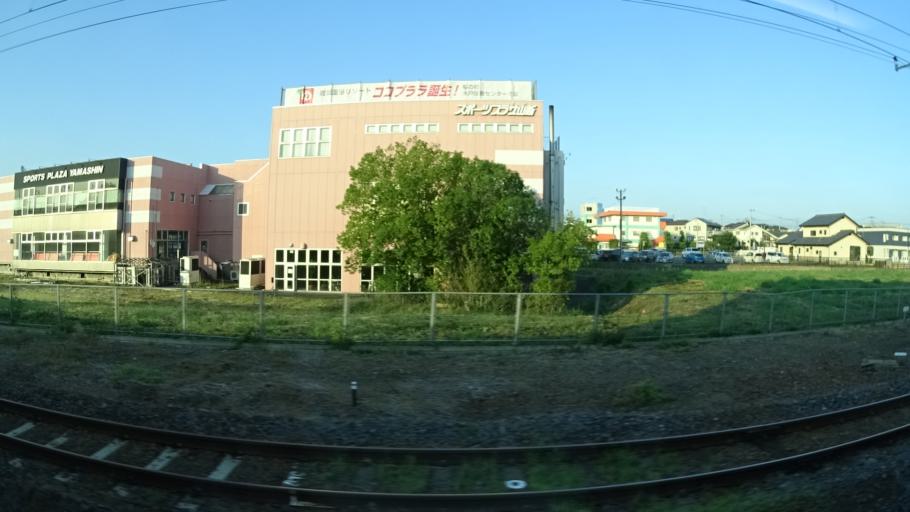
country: JP
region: Ibaraki
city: Ishioka
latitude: 36.1931
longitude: 140.2787
